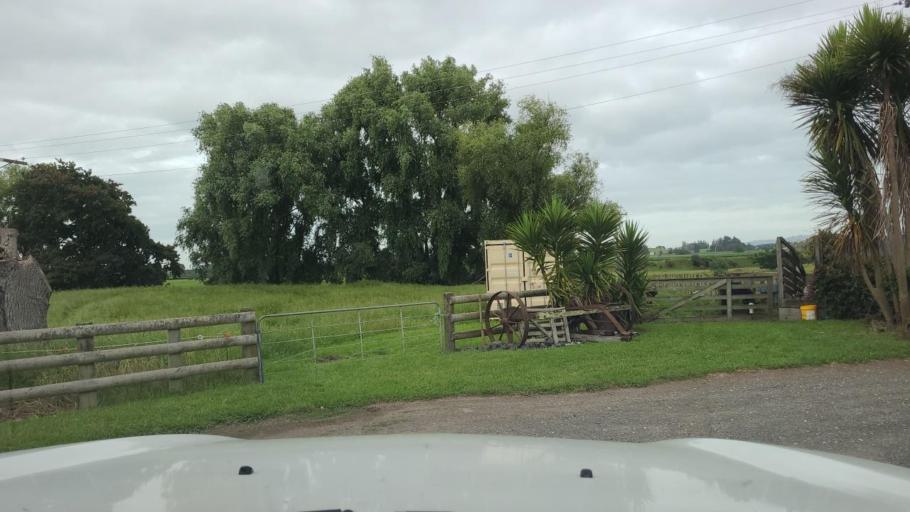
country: NZ
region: Waikato
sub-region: Hauraki District
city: Paeroa
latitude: -37.5730
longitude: 175.6646
